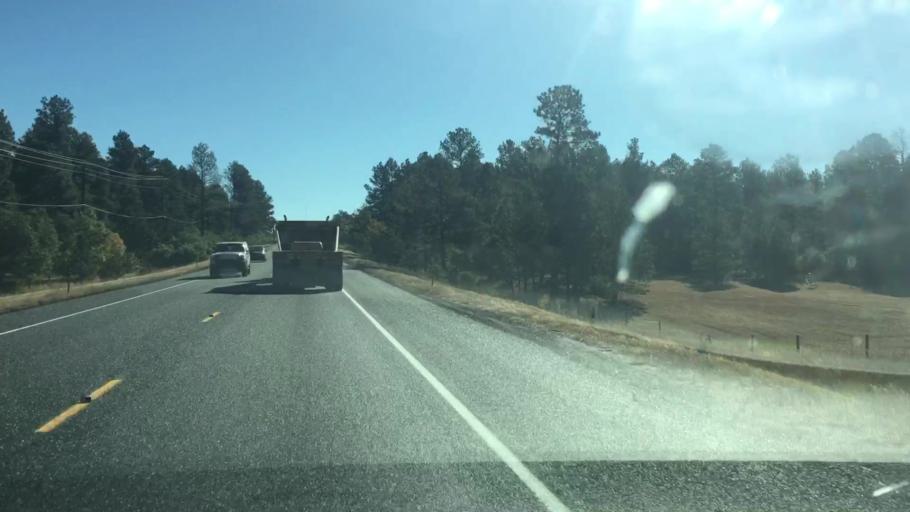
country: US
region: Colorado
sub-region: Elbert County
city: Ponderosa Park
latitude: 39.3795
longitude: -104.7143
